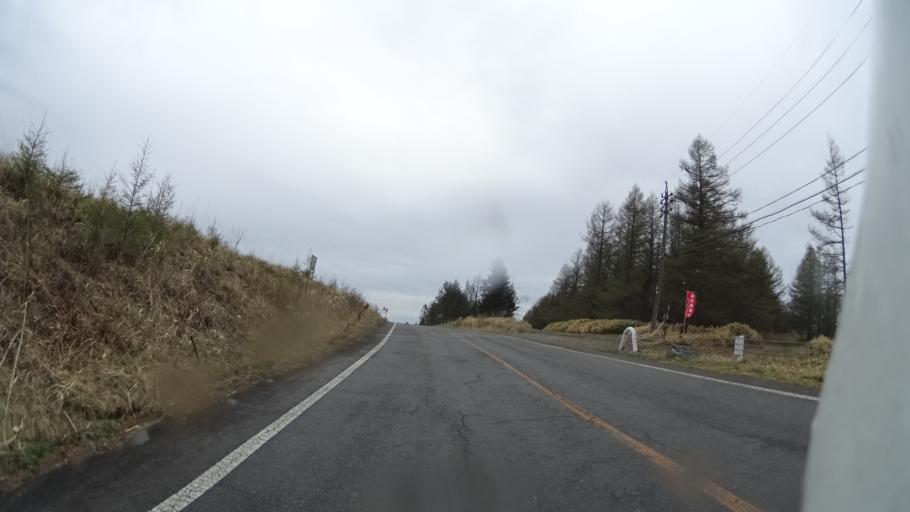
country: JP
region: Nagano
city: Suwa
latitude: 36.1026
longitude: 138.1713
